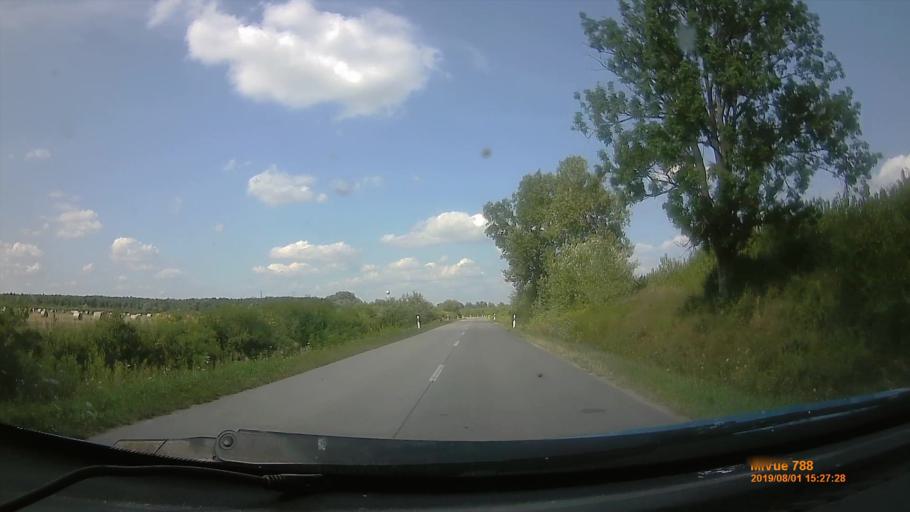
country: HU
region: Baranya
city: Sellye
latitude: 45.9066
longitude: 17.8629
